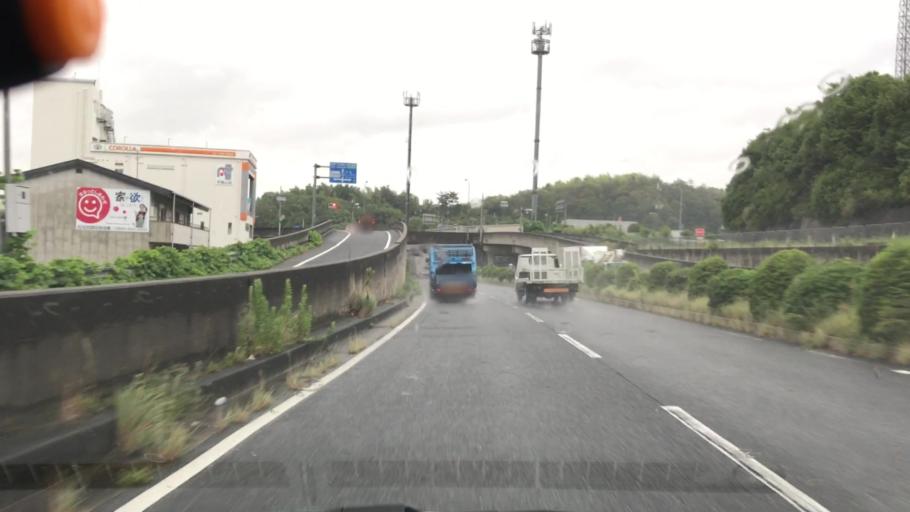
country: JP
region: Nara
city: Nara-shi
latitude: 34.7095
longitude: 135.8074
